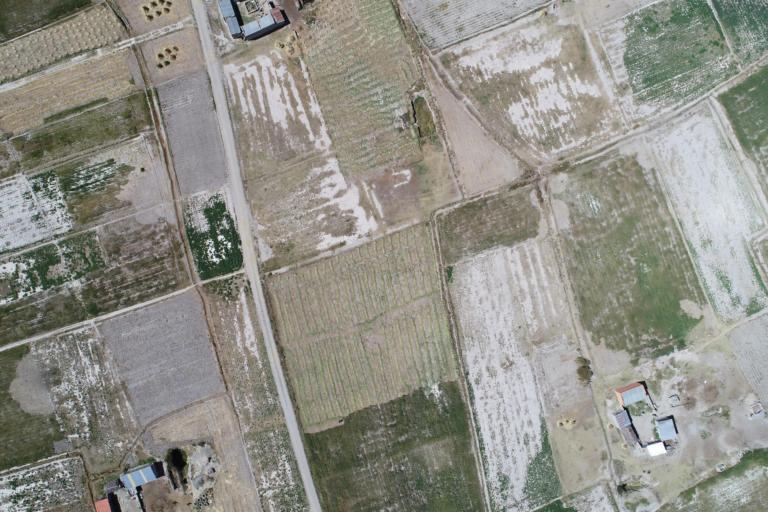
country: BO
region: La Paz
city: Achacachi
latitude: -16.0156
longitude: -68.7225
